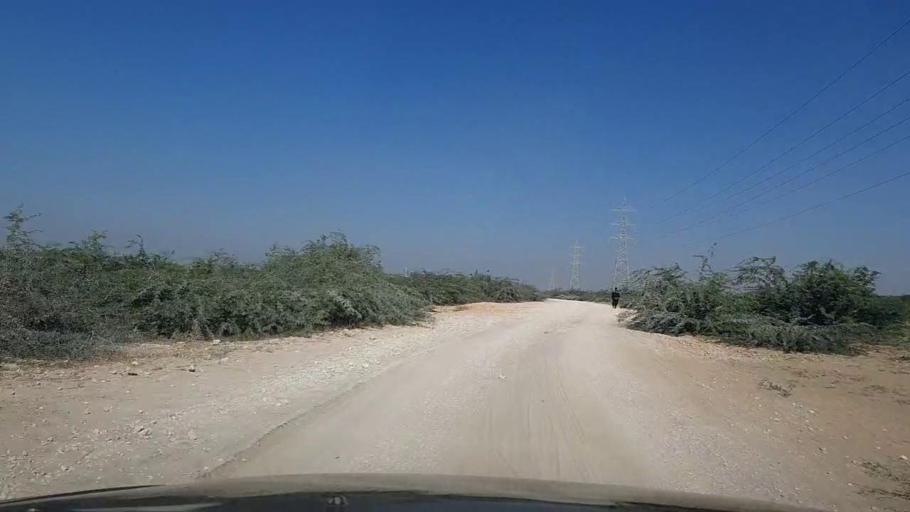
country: PK
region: Sindh
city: Thatta
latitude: 24.6275
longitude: 67.8342
